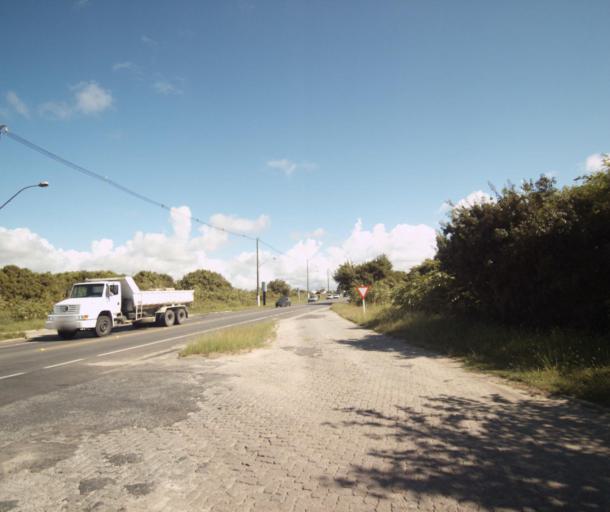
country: BR
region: Rio Grande do Sul
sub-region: Pelotas
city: Pelotas
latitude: -31.7531
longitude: -52.3587
